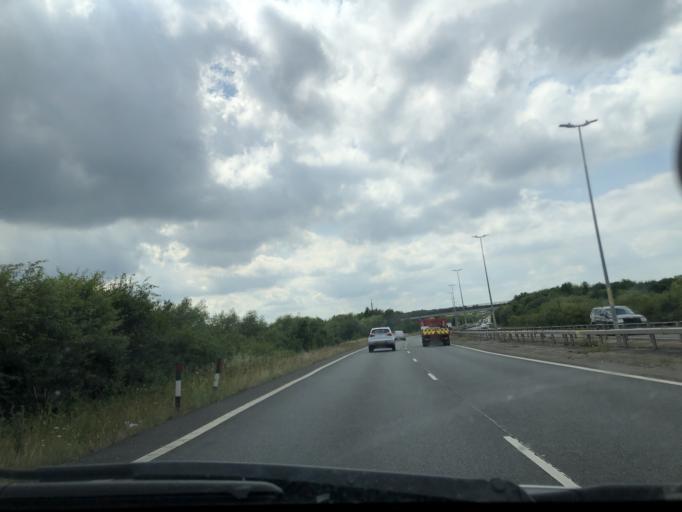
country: GB
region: England
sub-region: Kent
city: Tankerton
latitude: 51.3387
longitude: 1.0532
